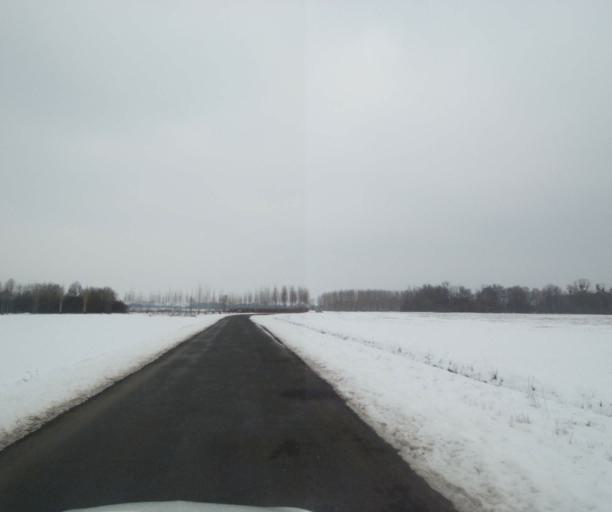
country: FR
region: Champagne-Ardenne
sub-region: Departement de la Haute-Marne
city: Saint-Dizier
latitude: 48.5687
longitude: 4.8909
